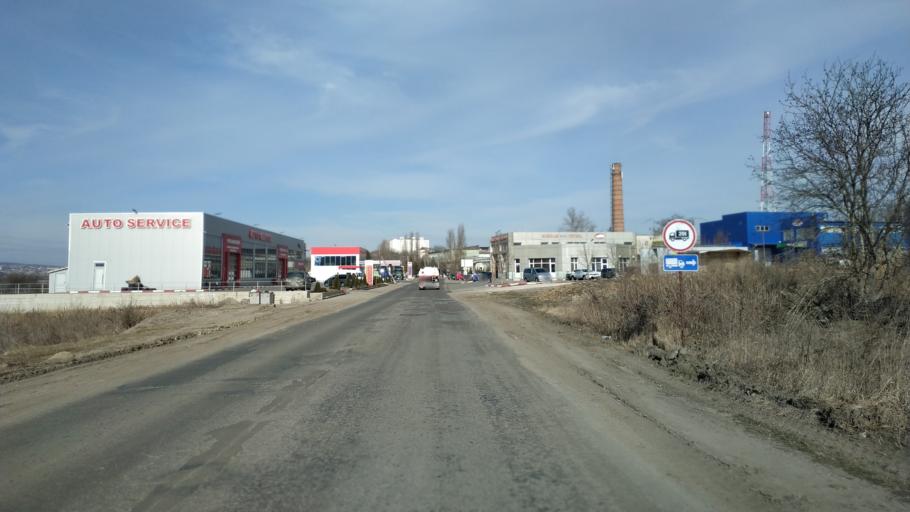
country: MD
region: Laloveni
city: Ialoveni
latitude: 46.9492
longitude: 28.7680
